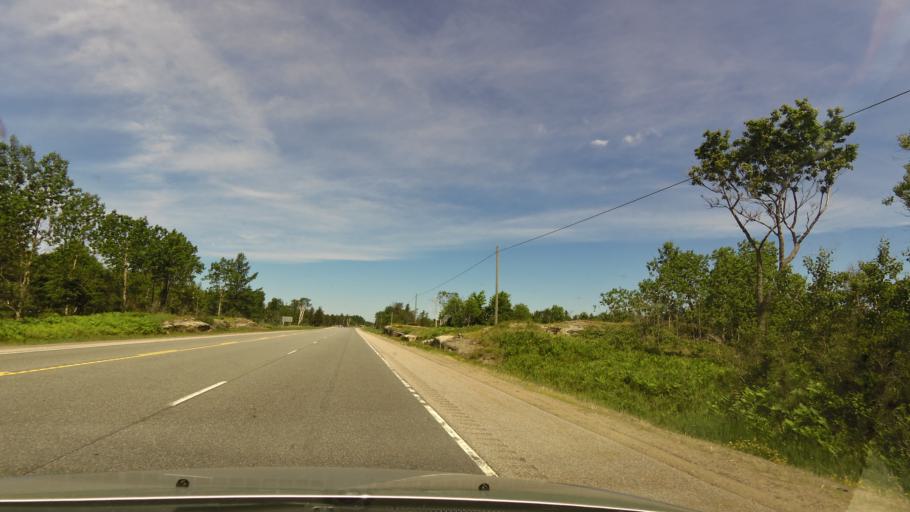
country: CA
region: Ontario
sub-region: Parry Sound District
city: Parry Sound
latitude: 45.4976
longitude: -80.2095
